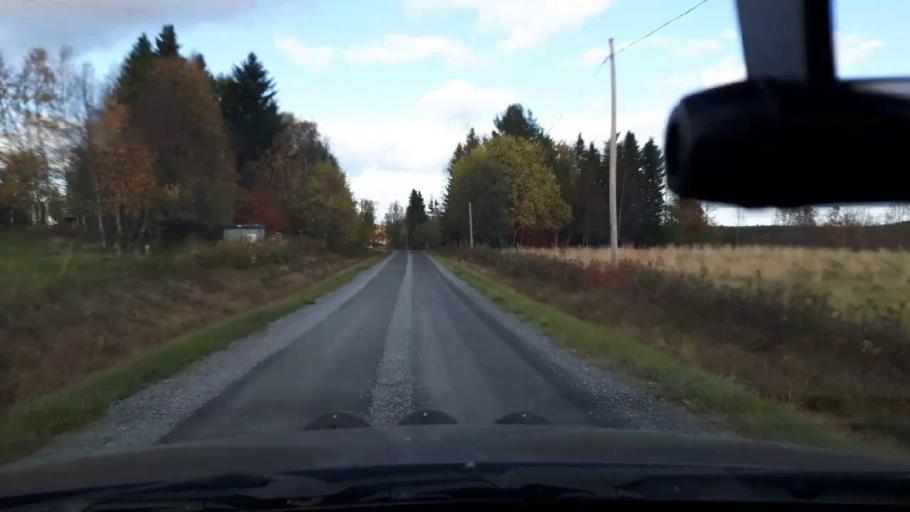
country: SE
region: Jaemtland
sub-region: Bergs Kommun
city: Hoverberg
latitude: 63.0545
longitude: 14.2387
